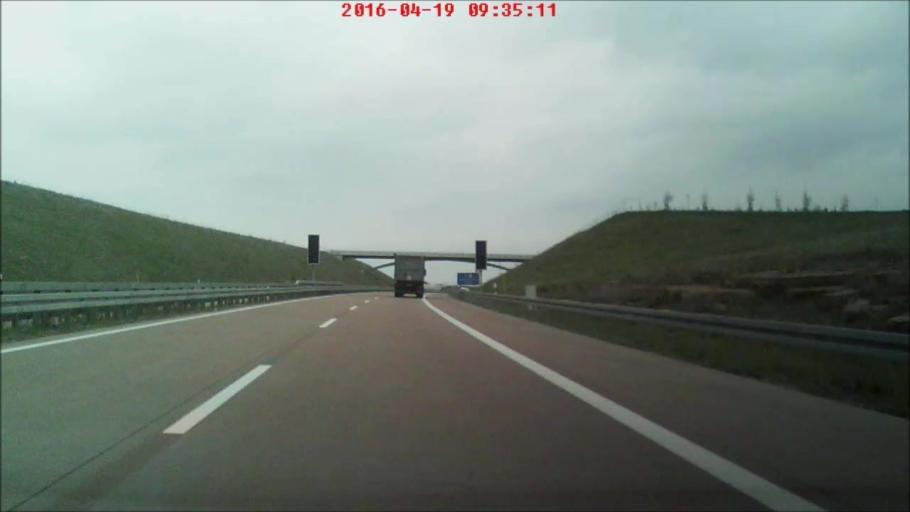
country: DE
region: Thuringia
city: Bretleben
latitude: 51.3186
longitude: 11.2394
